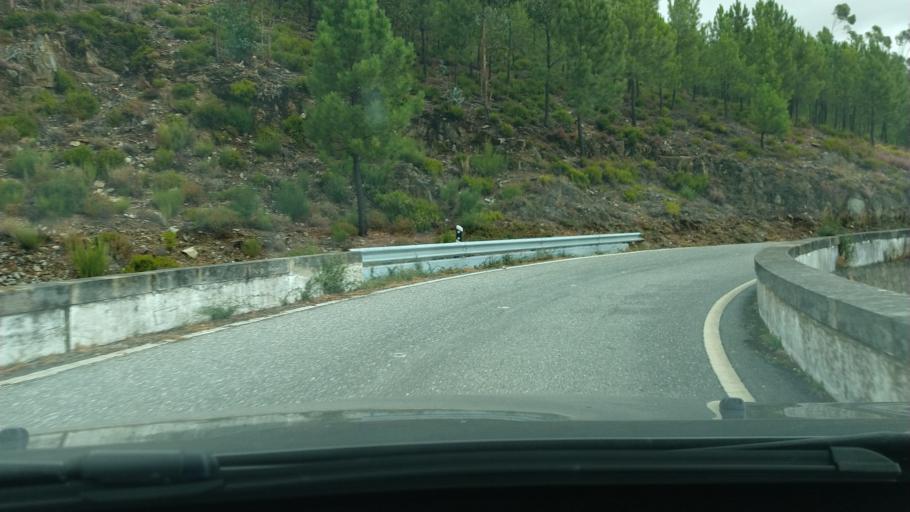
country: PT
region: Castelo Branco
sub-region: Covilha
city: Covilha
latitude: 40.2389
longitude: -7.6604
